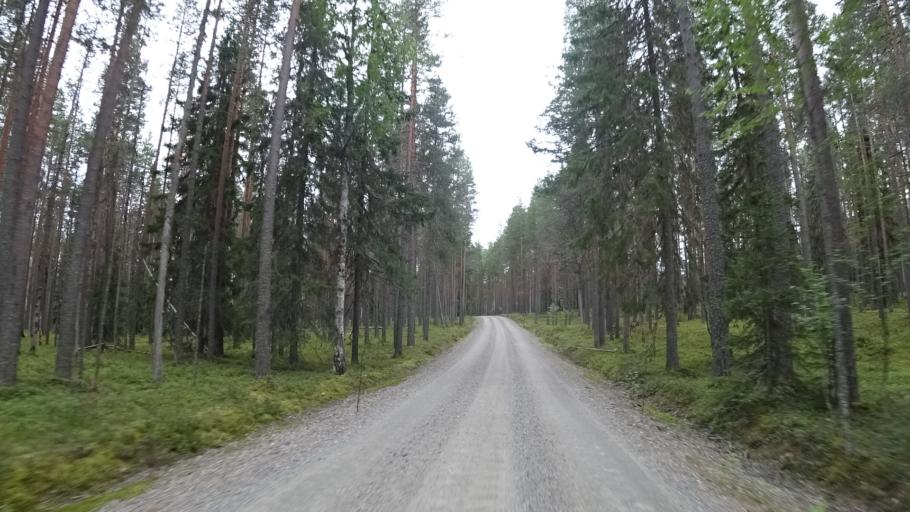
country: FI
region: North Karelia
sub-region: Joensuu
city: Ilomantsi
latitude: 62.5873
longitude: 31.1693
